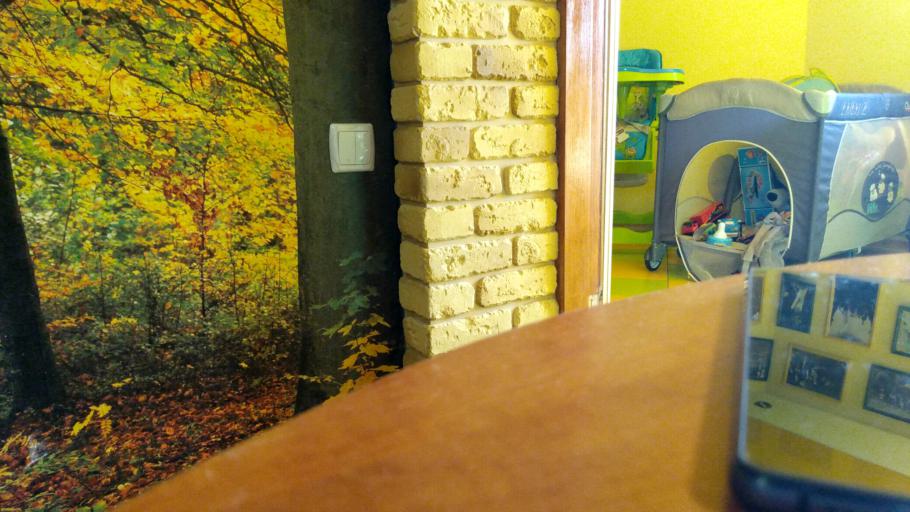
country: RU
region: Tverskaya
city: Likhoslavl'
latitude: 57.2244
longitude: 35.4745
